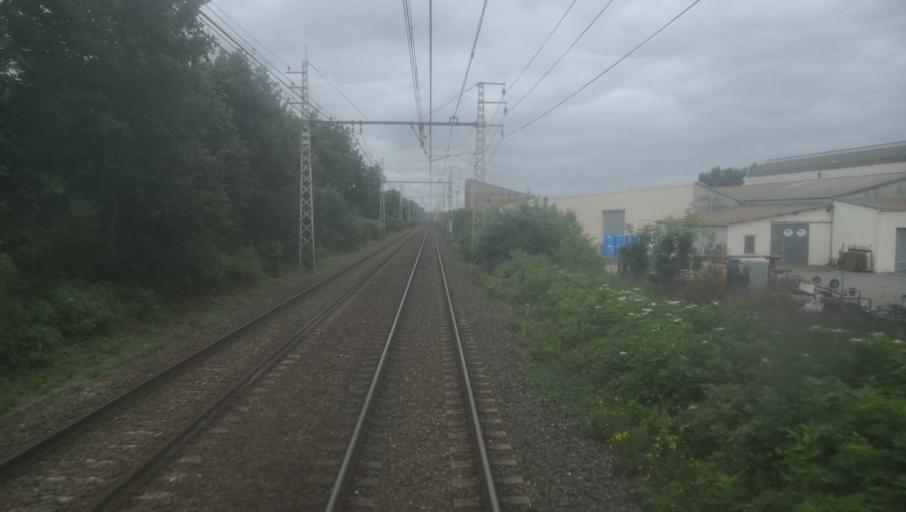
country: FR
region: Midi-Pyrenees
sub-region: Departement de la Haute-Garonne
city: Lespinasse
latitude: 43.7126
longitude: 1.3855
